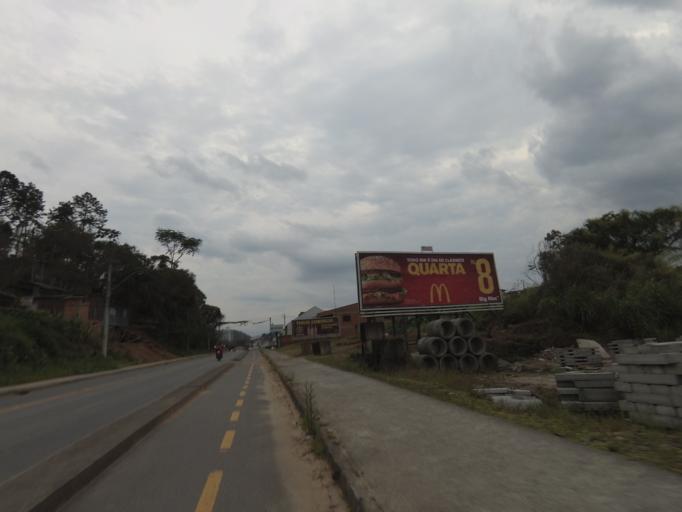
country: BR
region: Santa Catarina
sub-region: Blumenau
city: Blumenau
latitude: -26.8876
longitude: -49.0631
